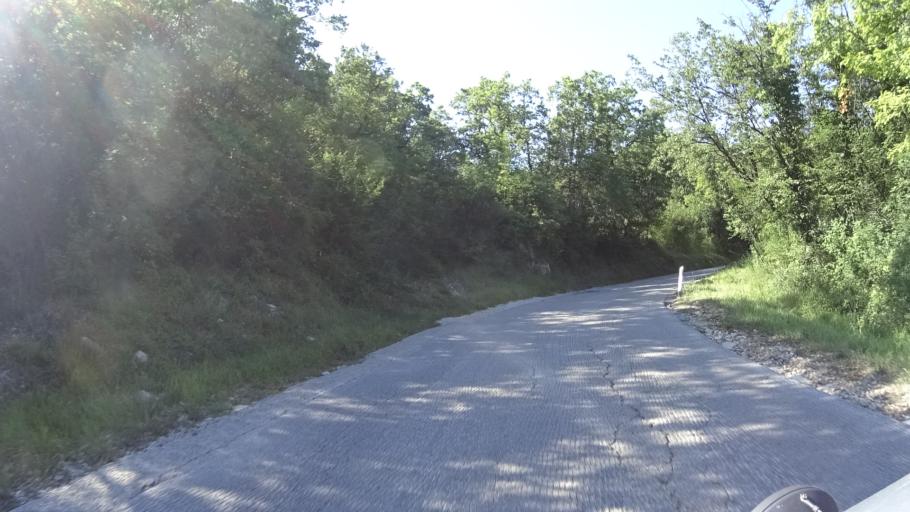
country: HR
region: Istarska
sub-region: Grad Labin
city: Labin
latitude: 45.0690
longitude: 14.1193
